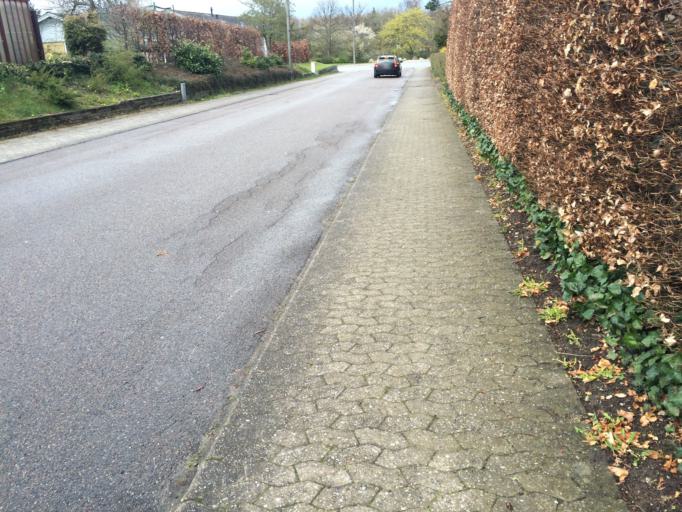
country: DK
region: Capital Region
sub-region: Ballerup Kommune
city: Ballerup
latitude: 55.7388
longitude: 12.3758
